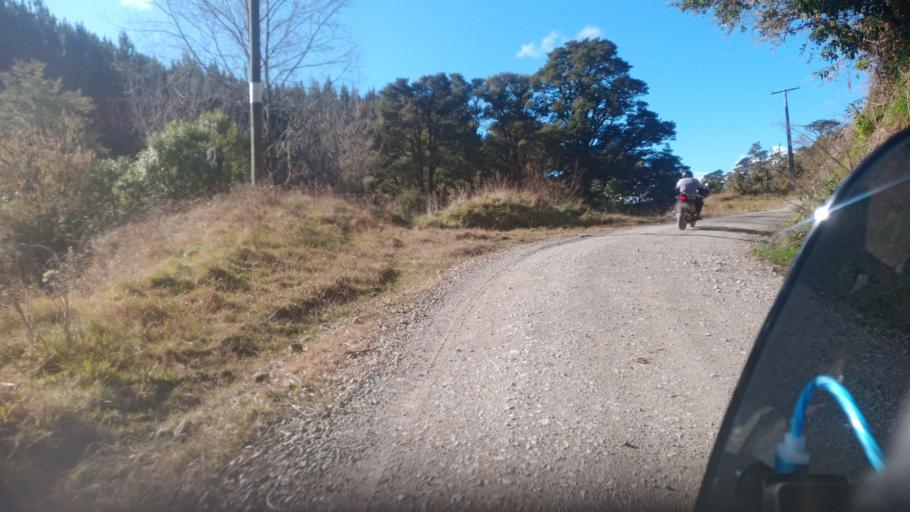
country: NZ
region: Hawke's Bay
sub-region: Wairoa District
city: Wairoa
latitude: -38.6637
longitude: 177.5102
